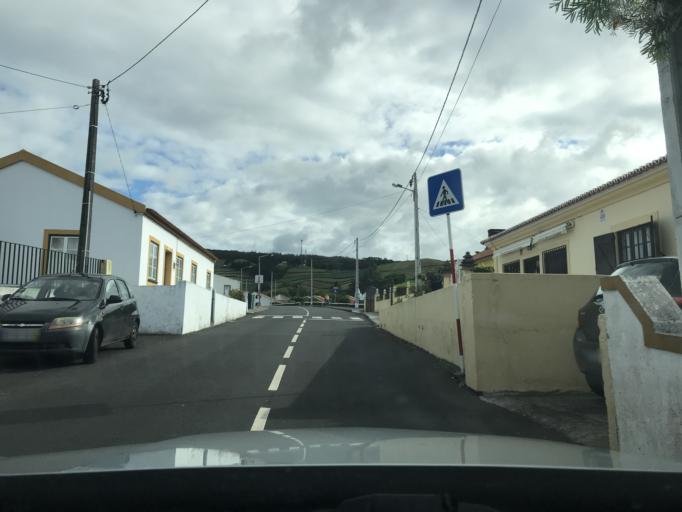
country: PT
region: Azores
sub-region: Angra do Heroismo
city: Angra do Heroismo
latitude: 38.6706
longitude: -27.2511
